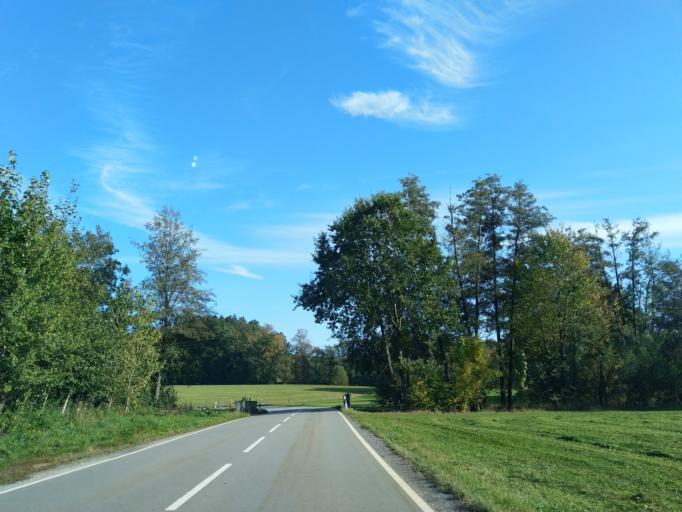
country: DE
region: Bavaria
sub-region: Lower Bavaria
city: Schwarzach
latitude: 48.9013
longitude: 12.8263
